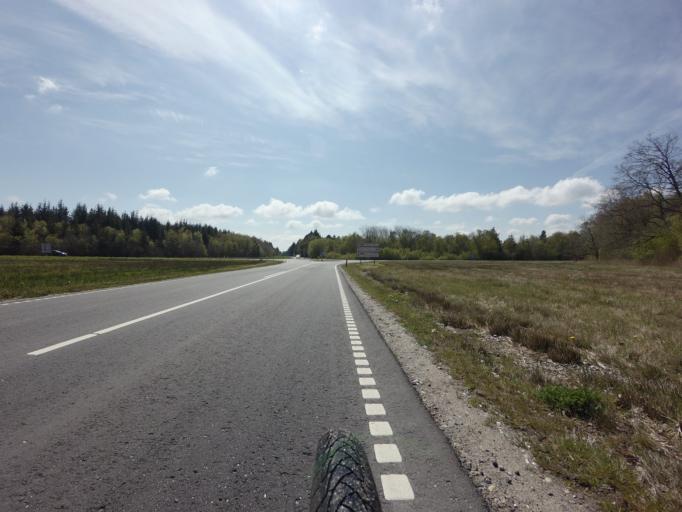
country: DK
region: North Denmark
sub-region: Jammerbugt Kommune
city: Brovst
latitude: 57.1634
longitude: 9.5752
